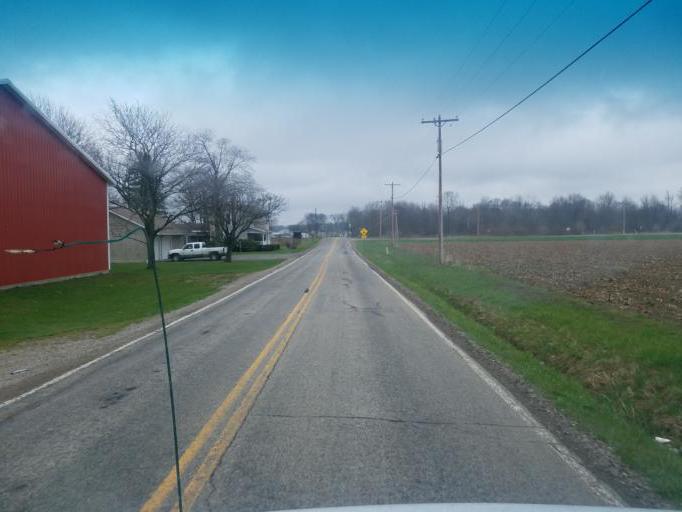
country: US
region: Ohio
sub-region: Richland County
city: Shelby
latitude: 40.9185
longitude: -82.6397
